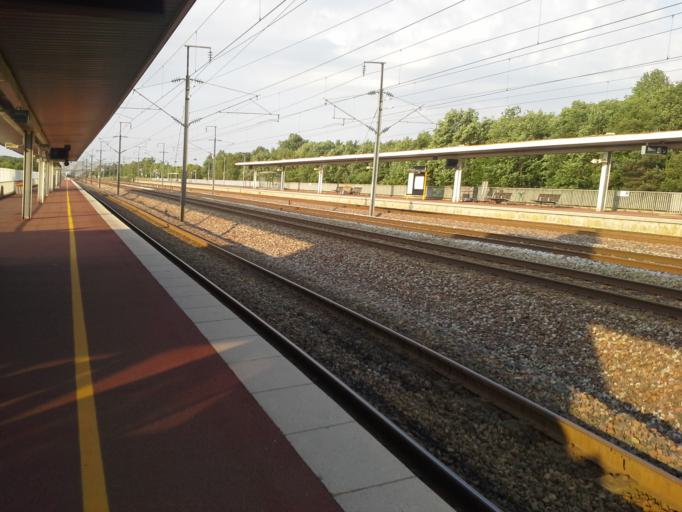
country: FR
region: Centre
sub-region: Departement du Loir-et-Cher
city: Villiers-sur-Loir
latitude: 47.8221
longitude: 1.0207
